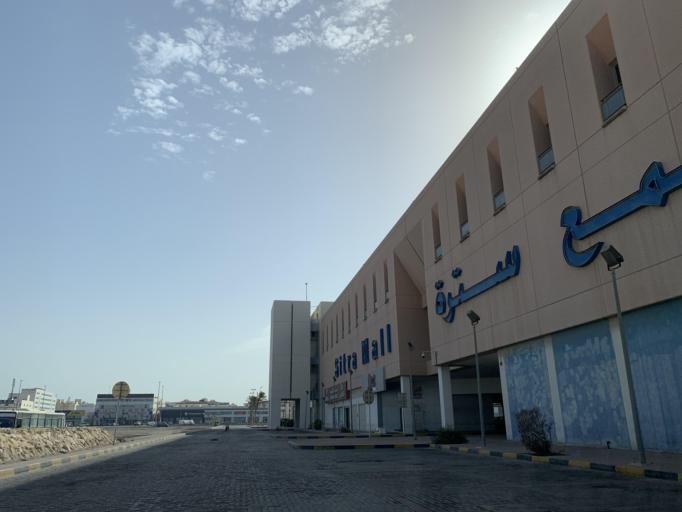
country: BH
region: Northern
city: Sitrah
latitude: 26.1694
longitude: 50.6002
